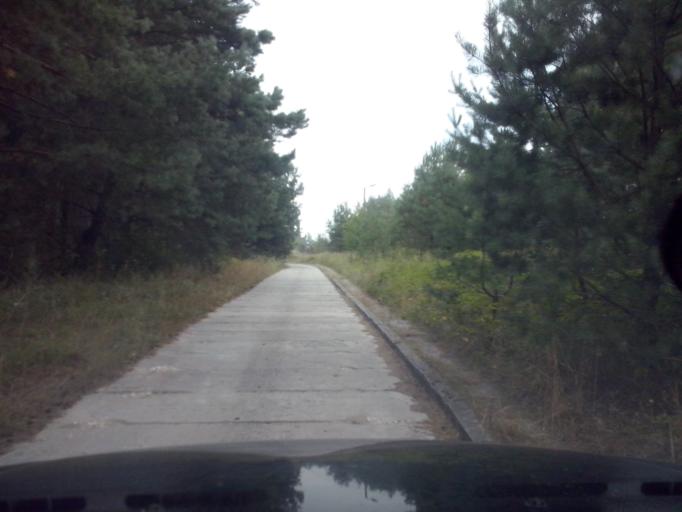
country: PL
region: Swietokrzyskie
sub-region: Powiat kielecki
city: Brzeziny
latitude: 50.7578
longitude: 20.5806
